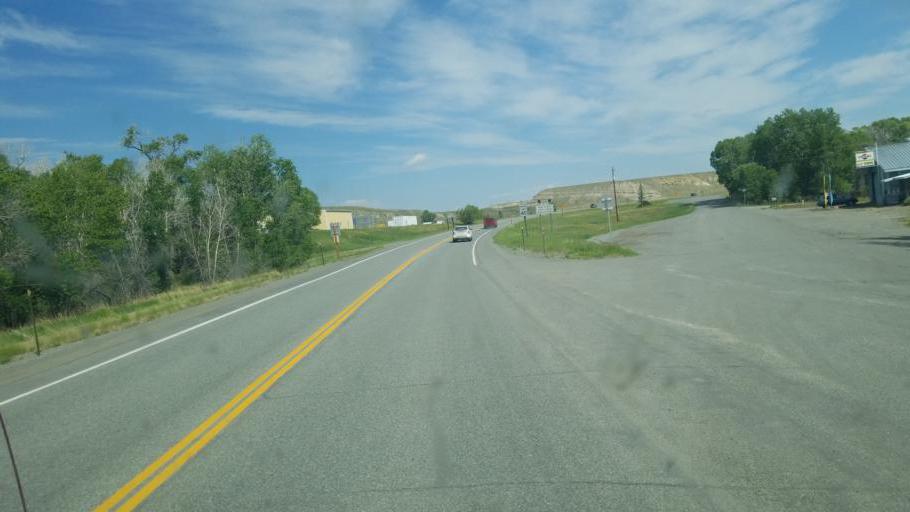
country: US
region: Wyoming
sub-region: Park County
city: Cody
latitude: 44.1593
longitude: -108.8737
